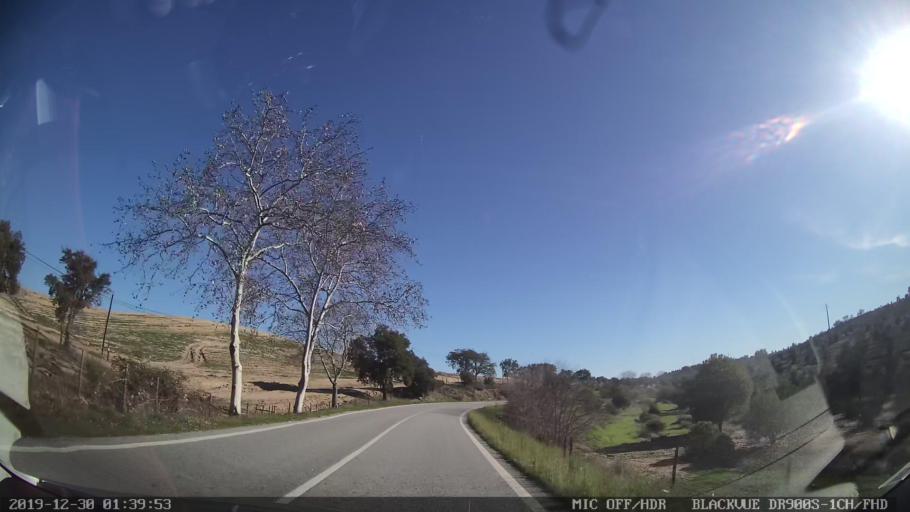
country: PT
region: Castelo Branco
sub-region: Idanha-A-Nova
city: Idanha-a-Nova
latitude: 39.8826
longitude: -7.1992
